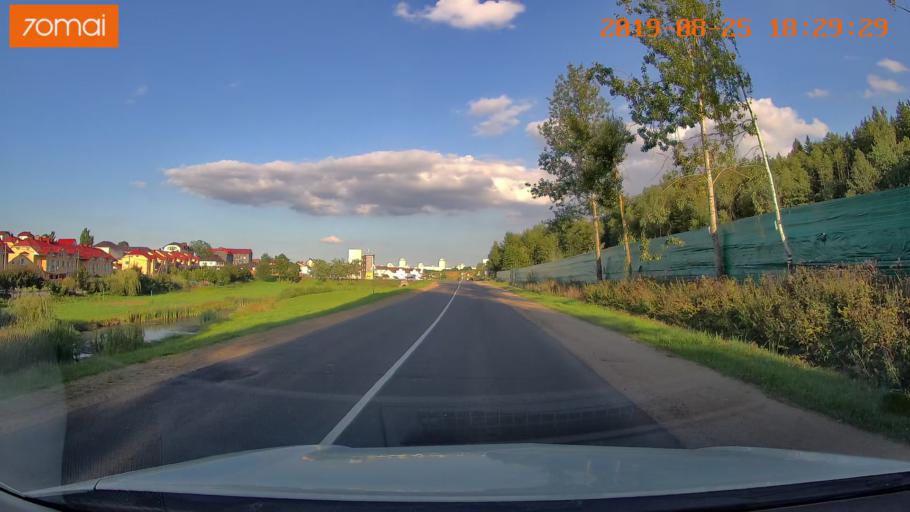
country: BY
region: Minsk
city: Zhdanovichy
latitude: 53.9155
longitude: 27.3867
